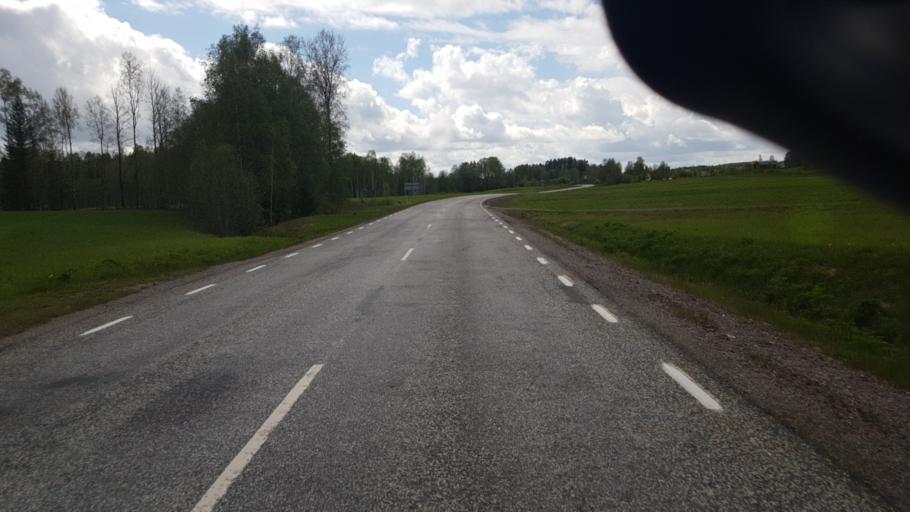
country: SE
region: Vaermland
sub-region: Arjangs Kommun
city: Arjaeng
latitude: 59.5616
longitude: 12.1214
